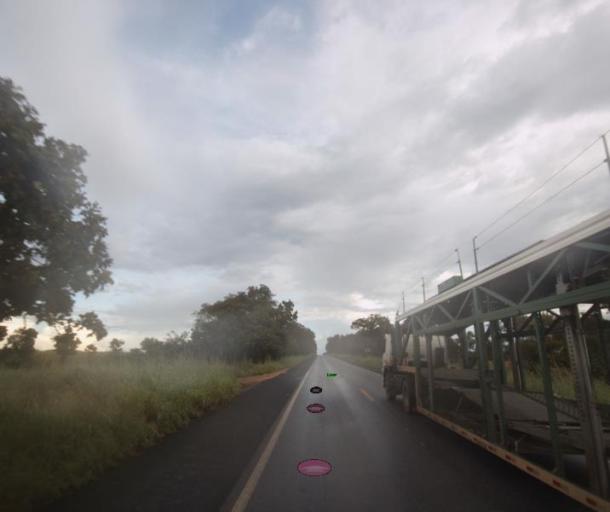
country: BR
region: Goias
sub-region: Porangatu
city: Porangatu
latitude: -13.8539
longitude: -49.0487
